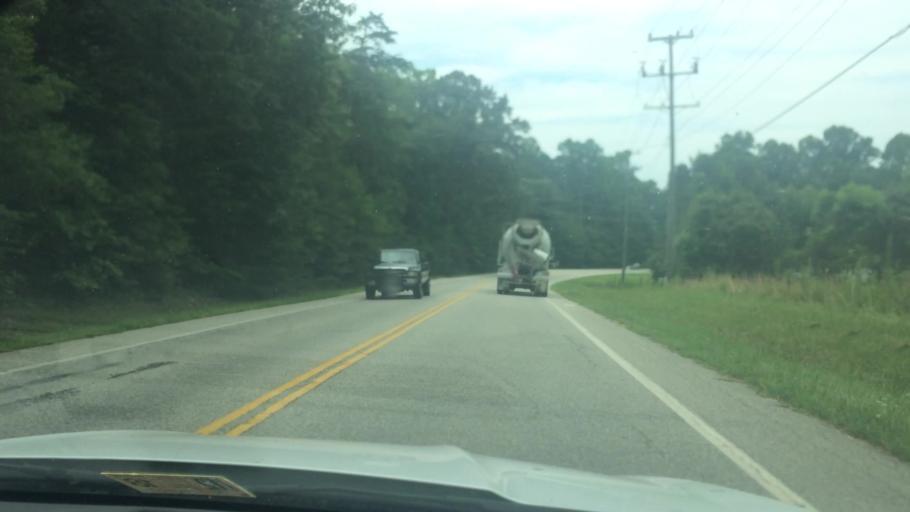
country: US
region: Virginia
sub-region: James City County
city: Williamsburg
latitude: 37.2912
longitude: -76.7992
